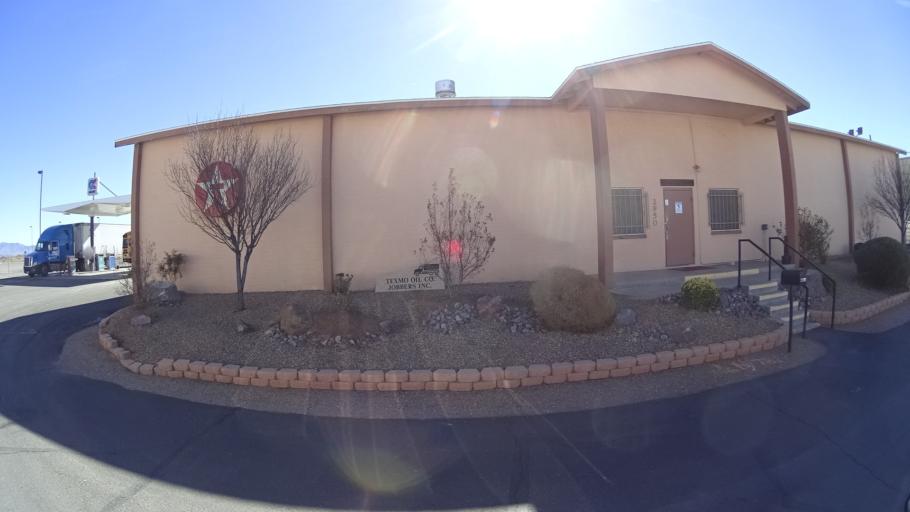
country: US
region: Arizona
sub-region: Mohave County
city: Kingman
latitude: 35.2118
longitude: -114.0142
